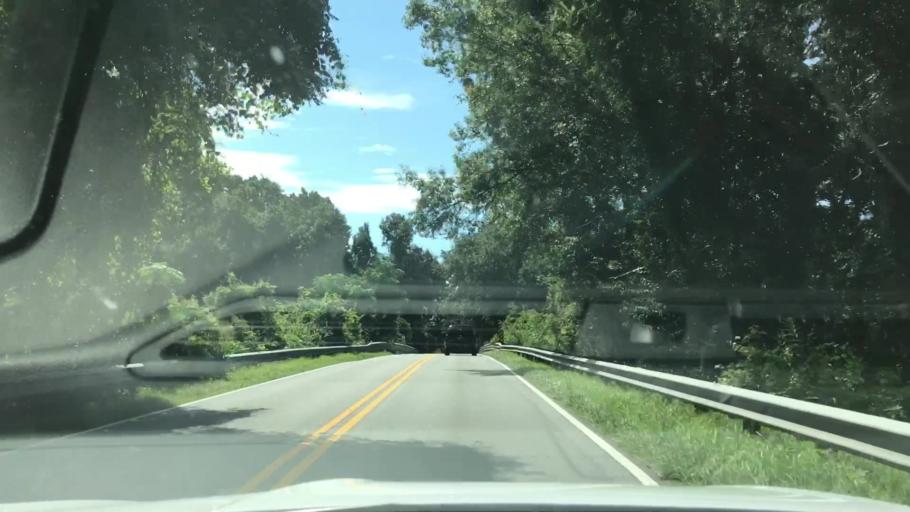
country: US
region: South Carolina
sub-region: Charleston County
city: Shell Point
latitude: 32.8422
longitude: -80.0566
